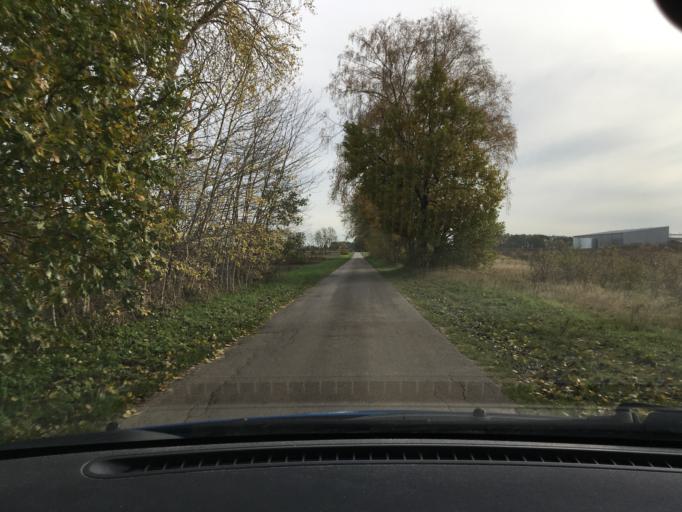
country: DE
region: Lower Saxony
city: Wittorf
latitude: 53.3167
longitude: 10.3749
